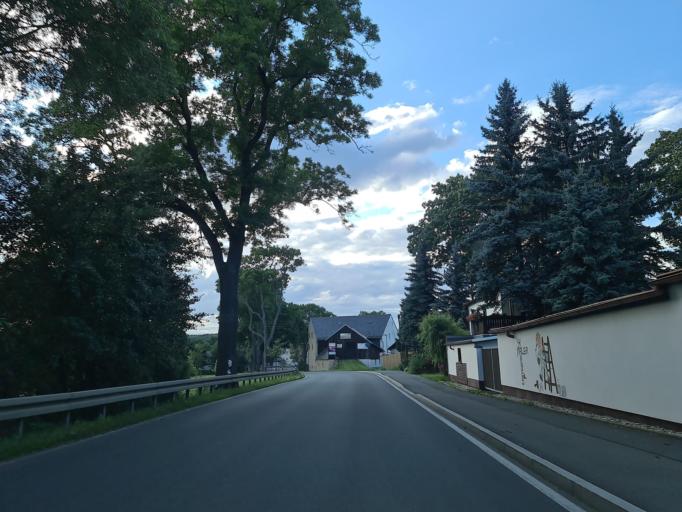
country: DE
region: Saxony
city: Pausa
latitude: 50.5746
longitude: 11.9930
